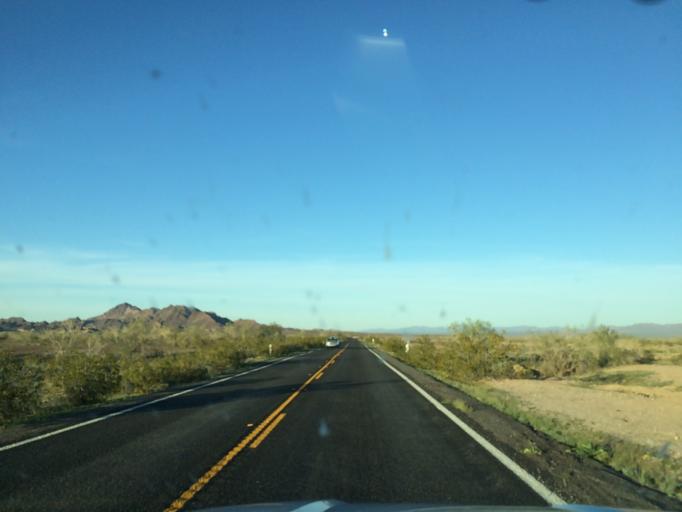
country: US
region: California
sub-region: Riverside County
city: Mesa Verde
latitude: 33.2616
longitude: -114.8051
